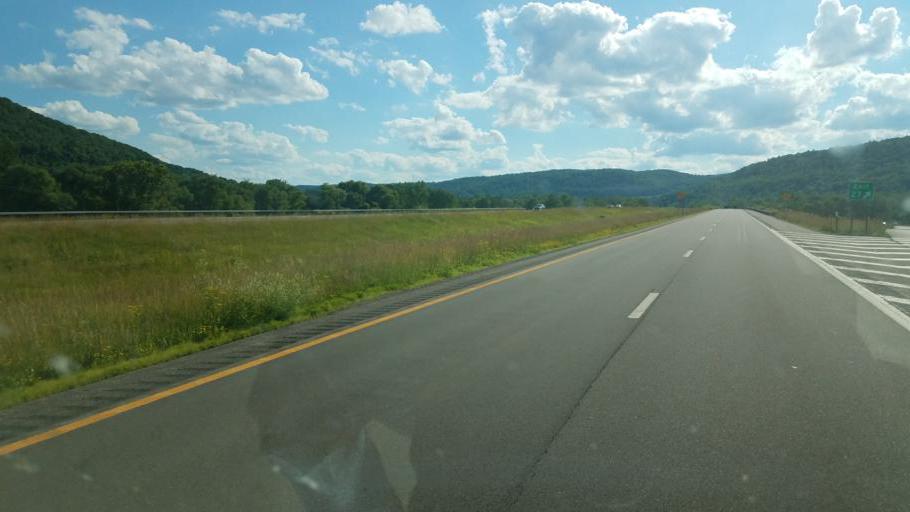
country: US
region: New York
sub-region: Cattaraugus County
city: Weston Mills
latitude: 42.1770
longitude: -78.3774
